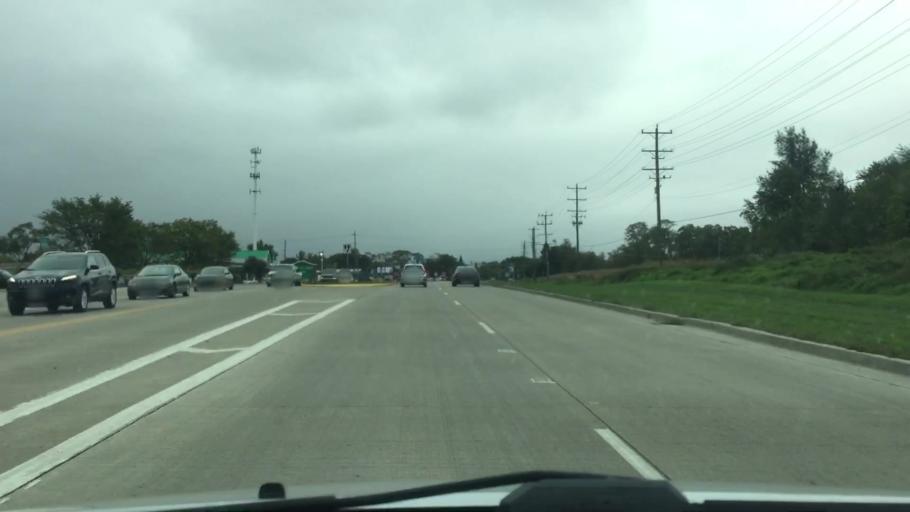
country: US
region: Illinois
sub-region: McHenry County
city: McHenry
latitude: 42.3240
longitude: -88.2743
